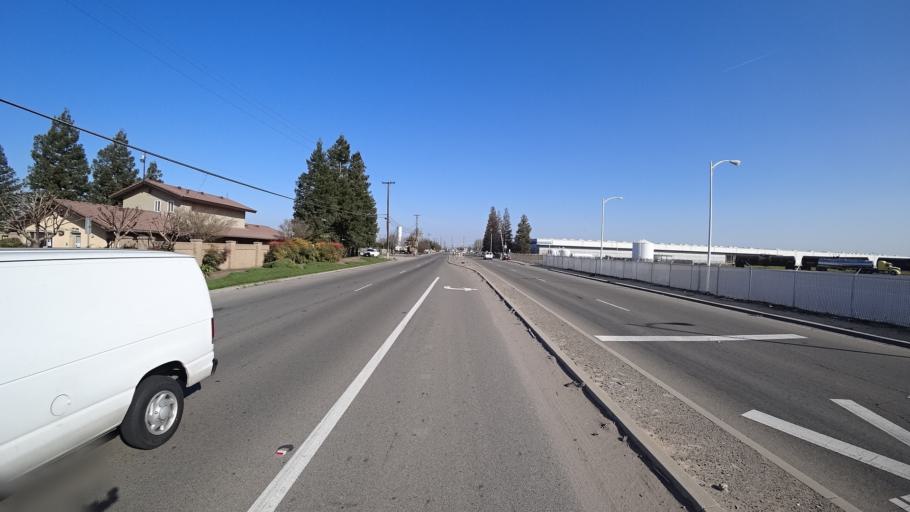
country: US
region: California
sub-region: Fresno County
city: Easton
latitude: 36.6875
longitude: -119.7366
